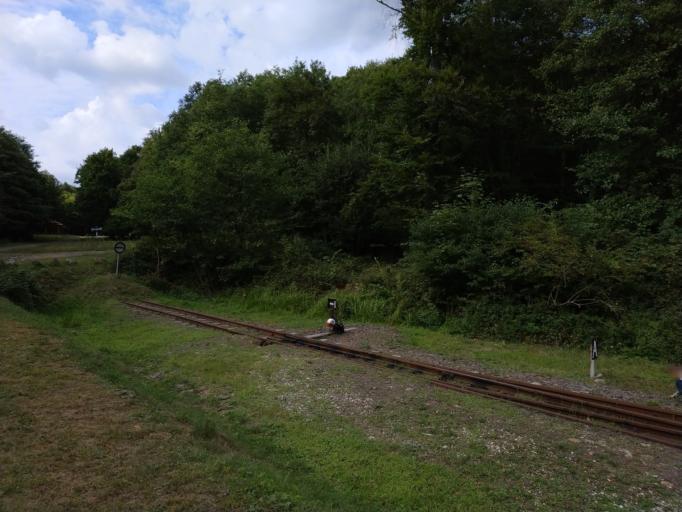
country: HU
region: Heves
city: Paradsasvar
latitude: 47.8833
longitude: 19.9153
